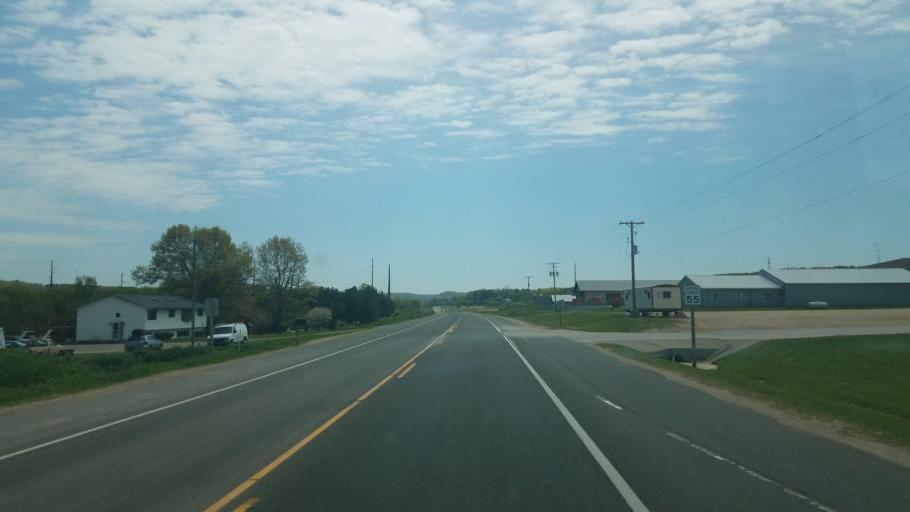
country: US
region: Wisconsin
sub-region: Monroe County
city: Tomah
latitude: 43.9538
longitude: -90.5048
